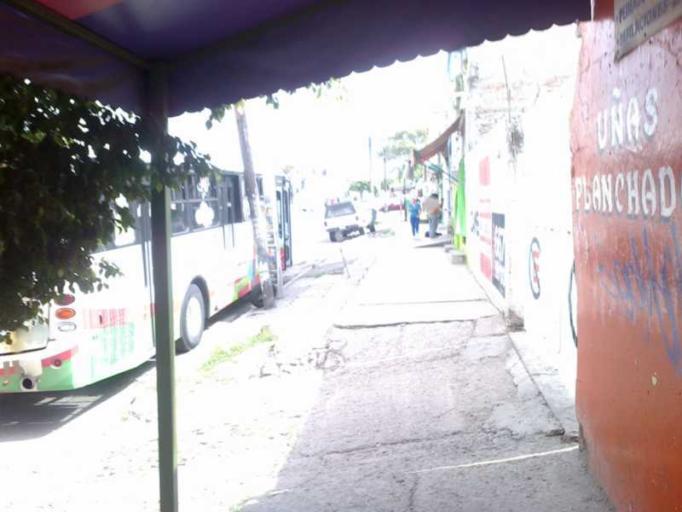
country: MX
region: Queretaro
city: San Jose el Alto
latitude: 20.6304
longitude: -100.3955
